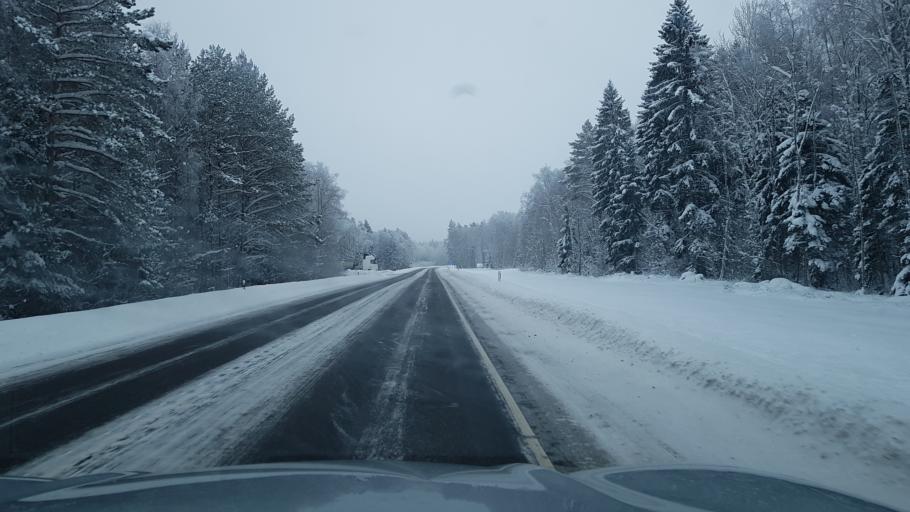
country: EE
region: Ida-Virumaa
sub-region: Johvi vald
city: Johvi
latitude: 59.2973
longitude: 27.3973
